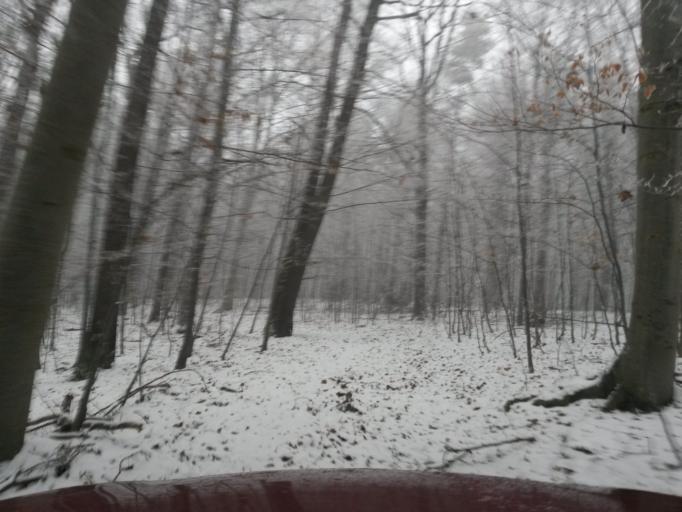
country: SK
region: Presovsky
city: Sabinov
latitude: 48.9763
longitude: 21.0922
